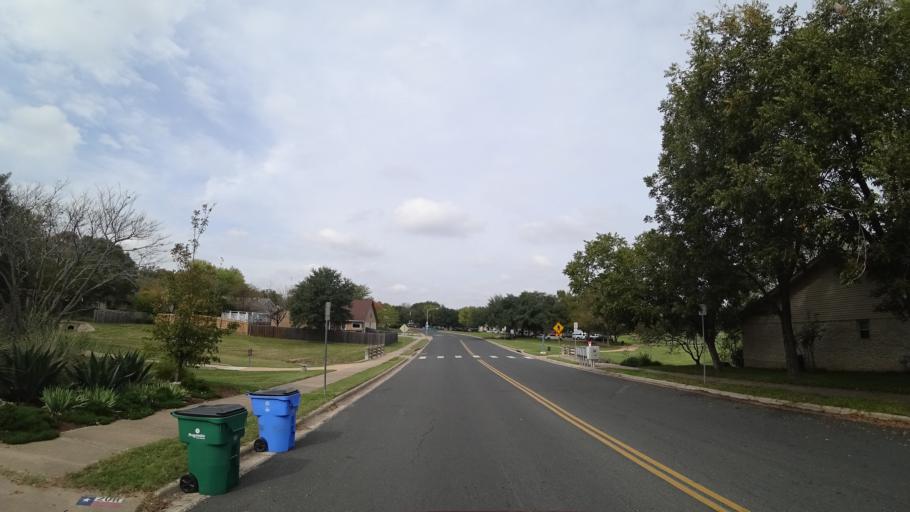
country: US
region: Texas
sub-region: Travis County
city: Wells Branch
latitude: 30.4407
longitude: -97.6788
